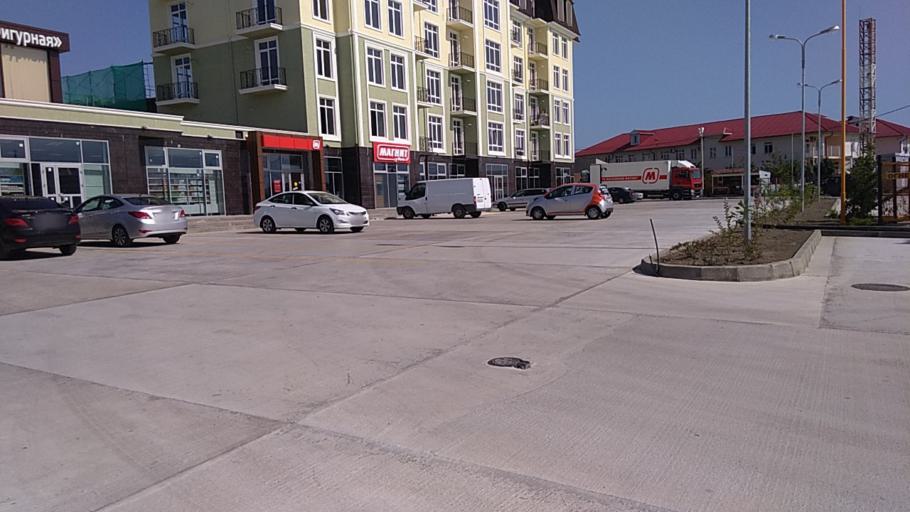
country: RU
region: Krasnodarskiy
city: Vysokoye
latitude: 43.3980
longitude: 39.9953
